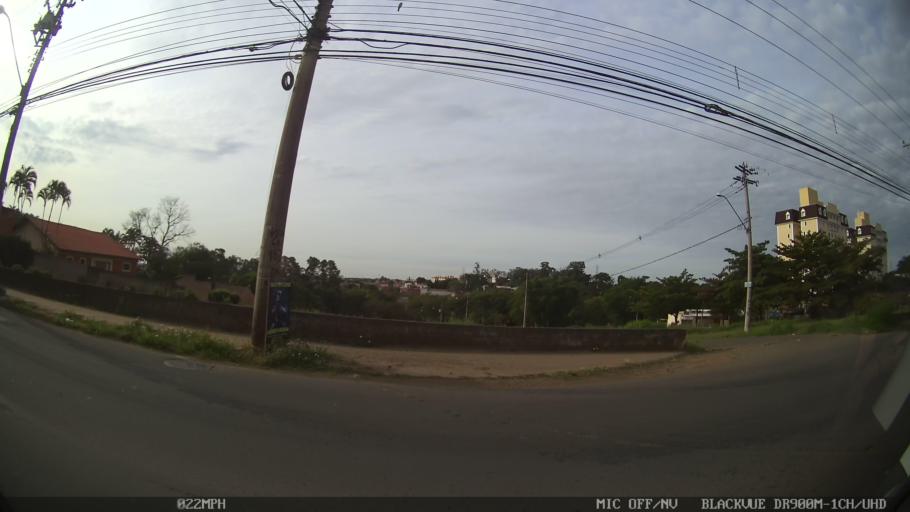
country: BR
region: Sao Paulo
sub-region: Piracicaba
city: Piracicaba
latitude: -22.7416
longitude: -47.6181
